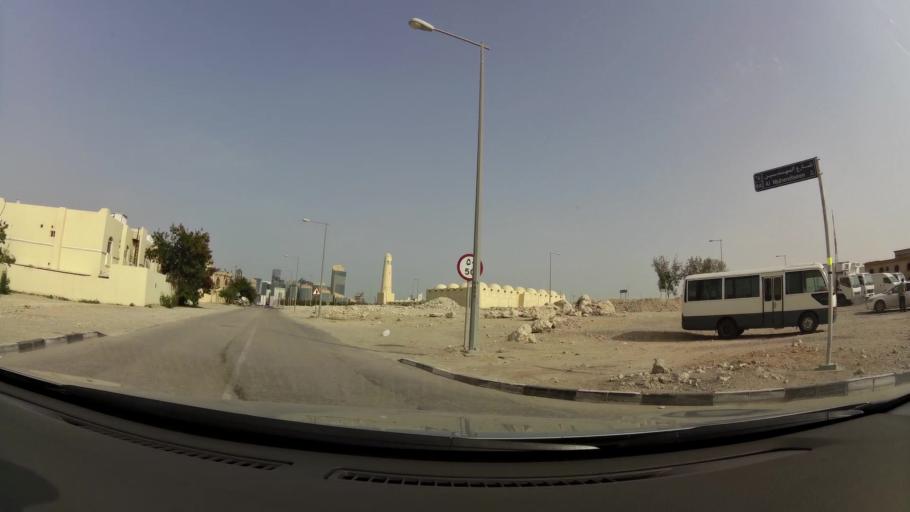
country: QA
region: Baladiyat ad Dawhah
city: Doha
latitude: 25.3189
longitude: 51.5012
